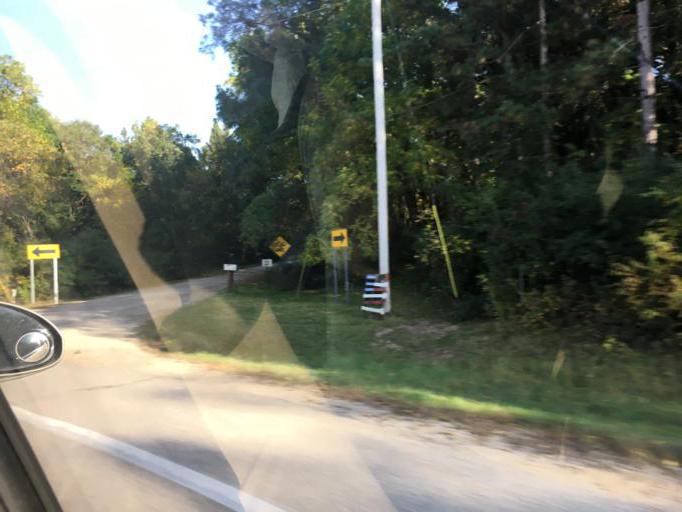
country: US
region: Minnesota
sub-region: Olmsted County
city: Rochester
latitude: 43.9924
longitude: -92.3890
